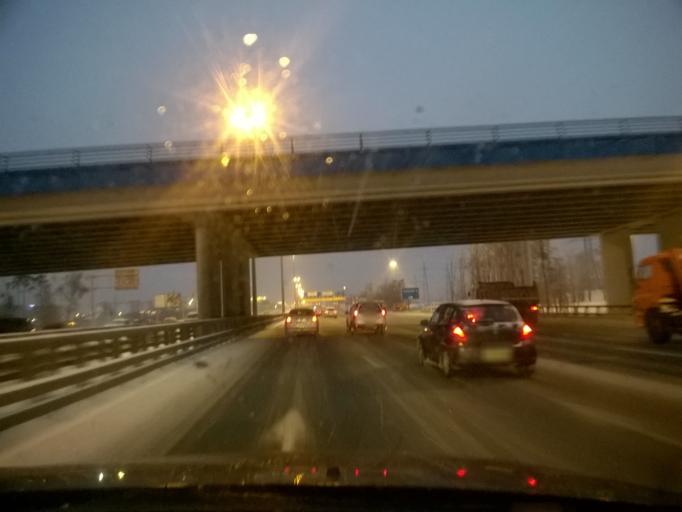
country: RU
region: Moskovskaya
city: Mosrentgen
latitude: 55.6273
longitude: 37.4237
